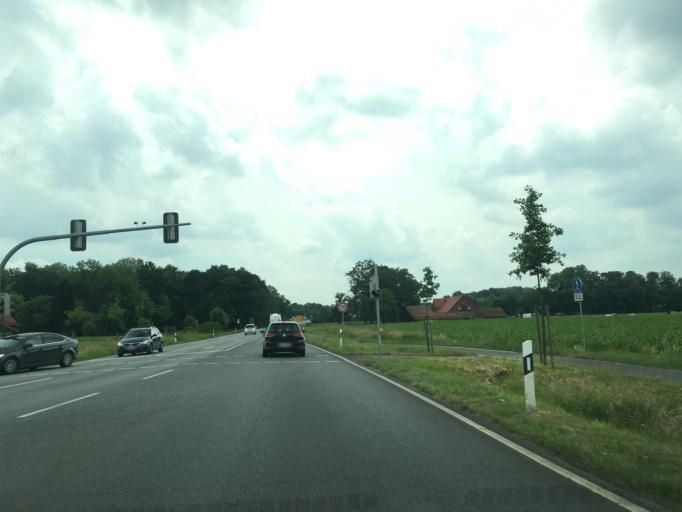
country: DE
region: North Rhine-Westphalia
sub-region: Regierungsbezirk Munster
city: Steinfurt
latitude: 52.1638
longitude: 7.3436
